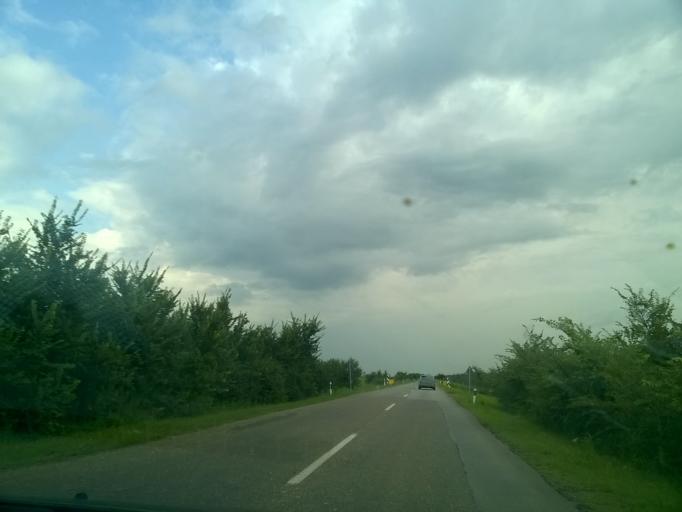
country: RS
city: Uzdin
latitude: 45.2315
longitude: 20.6263
